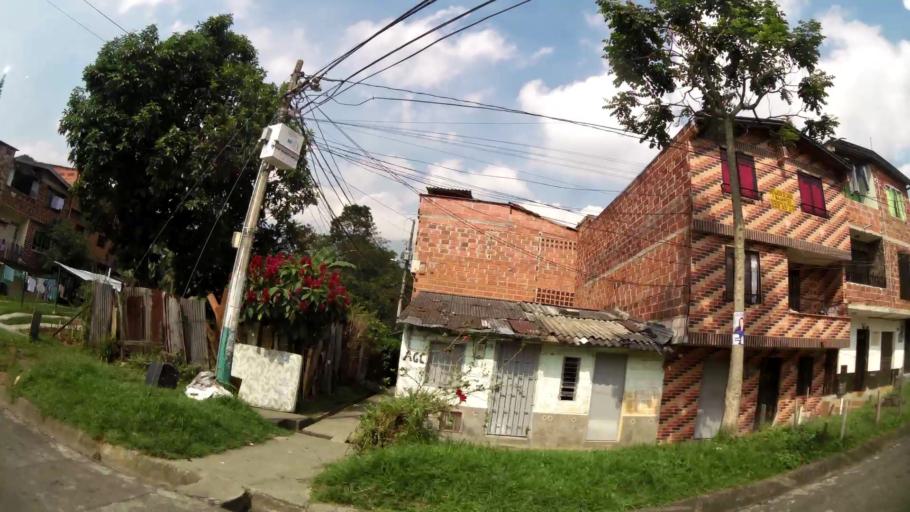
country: CO
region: Antioquia
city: La Estrella
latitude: 6.1743
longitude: -75.6382
